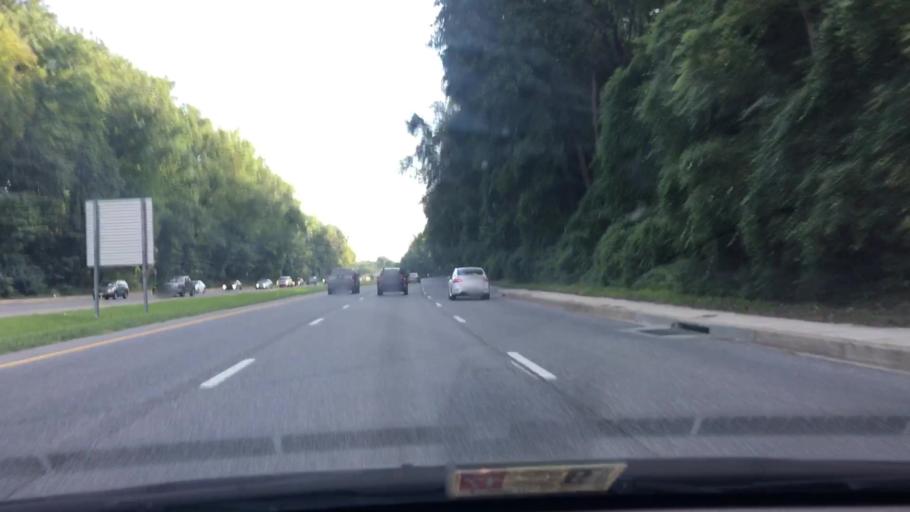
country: US
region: Maryland
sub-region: Montgomery County
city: Rossmoor
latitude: 39.0995
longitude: -77.0777
